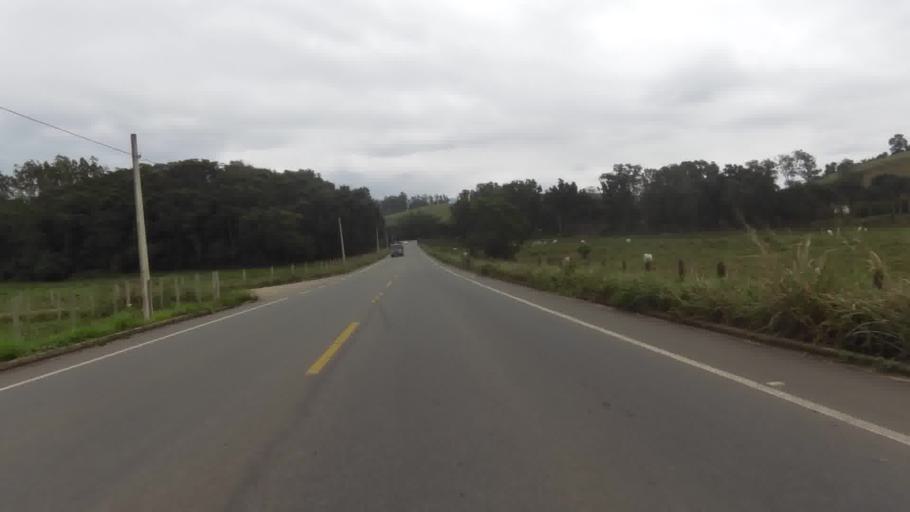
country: BR
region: Espirito Santo
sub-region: Iconha
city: Iconha
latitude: -20.7740
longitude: -40.7603
